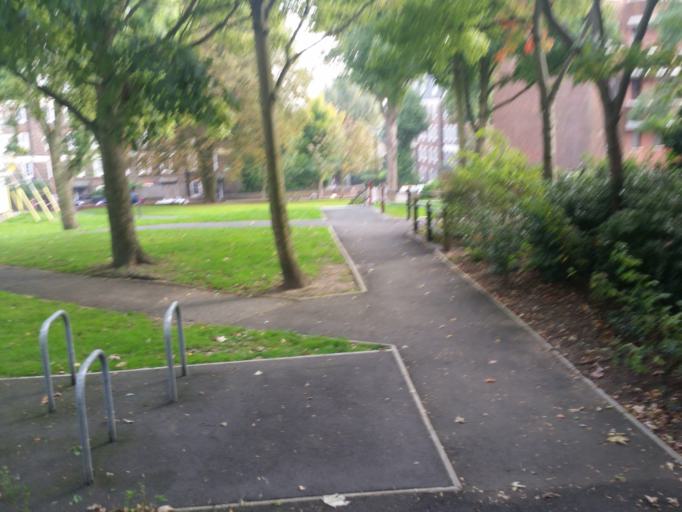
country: GB
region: England
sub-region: Greater London
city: Crouch End
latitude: 51.5735
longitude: -0.1229
